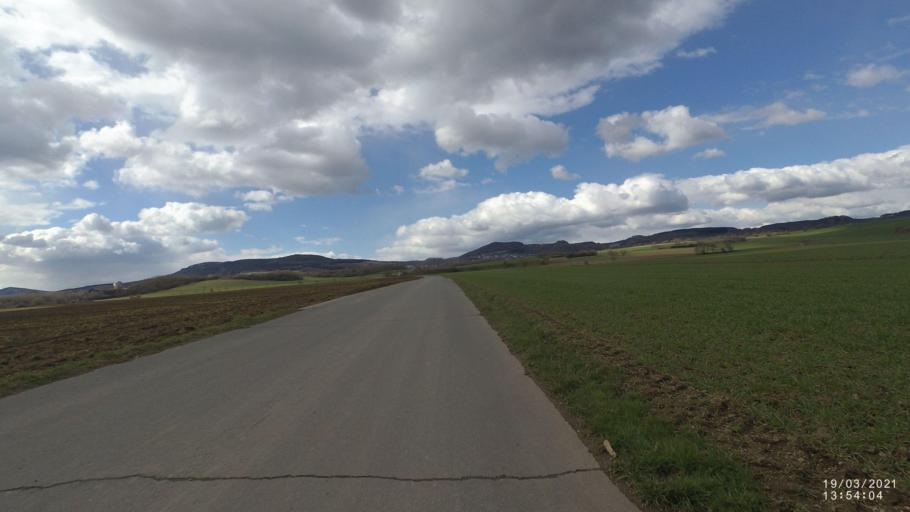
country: DE
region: Rheinland-Pfalz
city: Kretz
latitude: 50.4017
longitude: 7.3564
